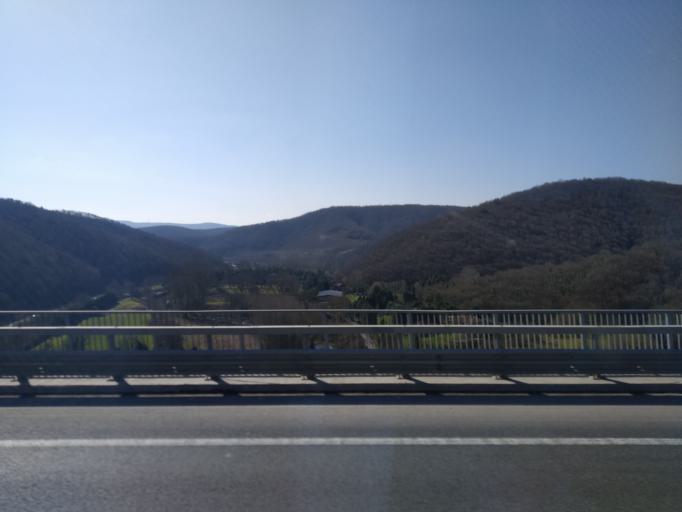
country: TR
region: Istanbul
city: Mahmut Sevket Pasa
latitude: 41.1538
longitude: 29.2675
